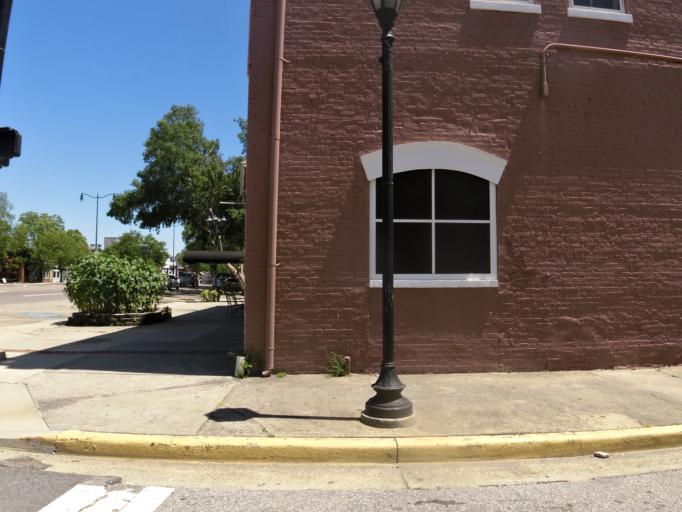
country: US
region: Georgia
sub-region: Richmond County
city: Augusta
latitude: 33.4737
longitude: -81.9617
